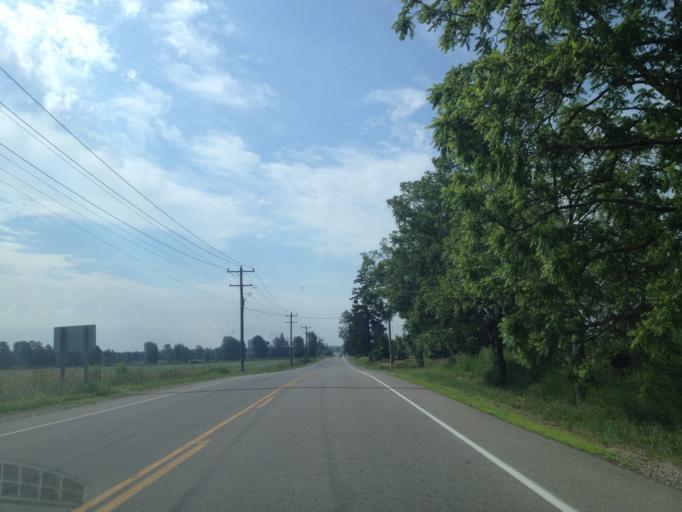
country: CA
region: Ontario
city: London
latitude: 43.0396
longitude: -81.3214
